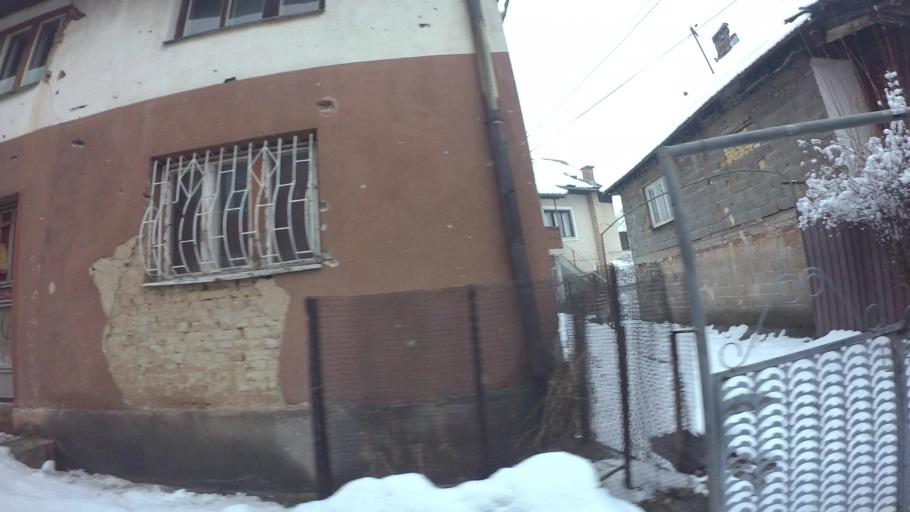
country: BA
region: Federation of Bosnia and Herzegovina
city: Kobilja Glava
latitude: 43.8500
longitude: 18.4261
